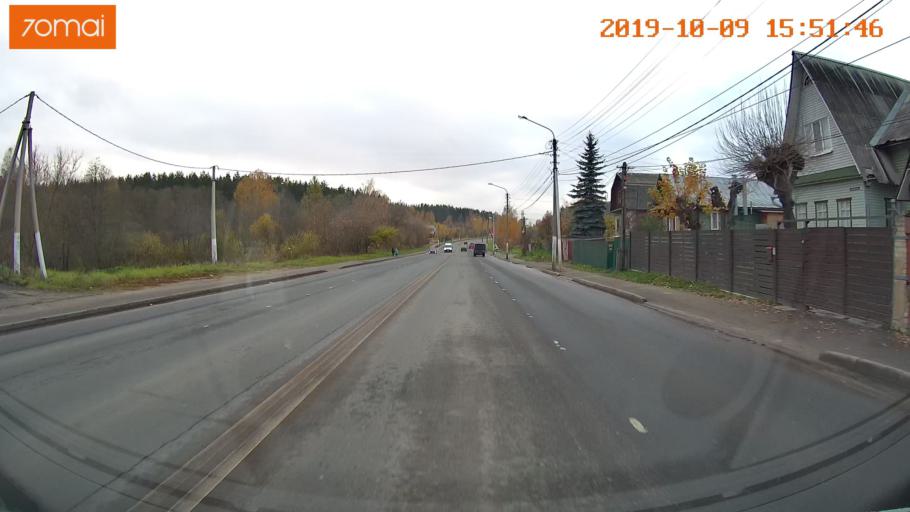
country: RU
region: Kostroma
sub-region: Kostromskoy Rayon
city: Kostroma
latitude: 57.7949
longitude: 40.9758
